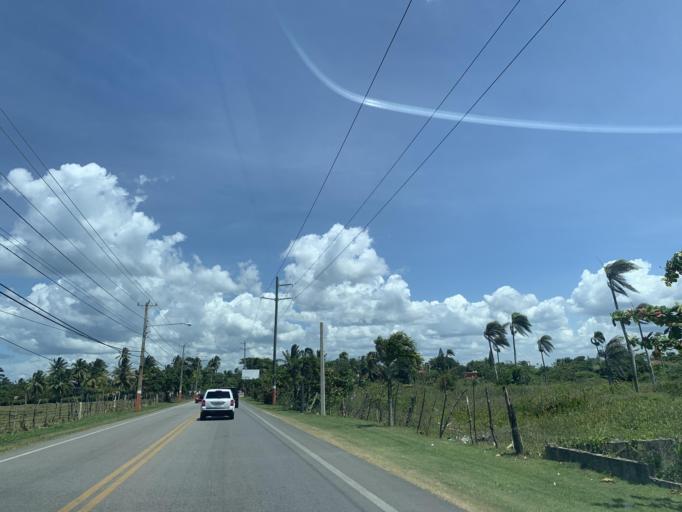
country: DO
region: Puerto Plata
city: Cabarete
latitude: 19.7381
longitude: -70.3908
